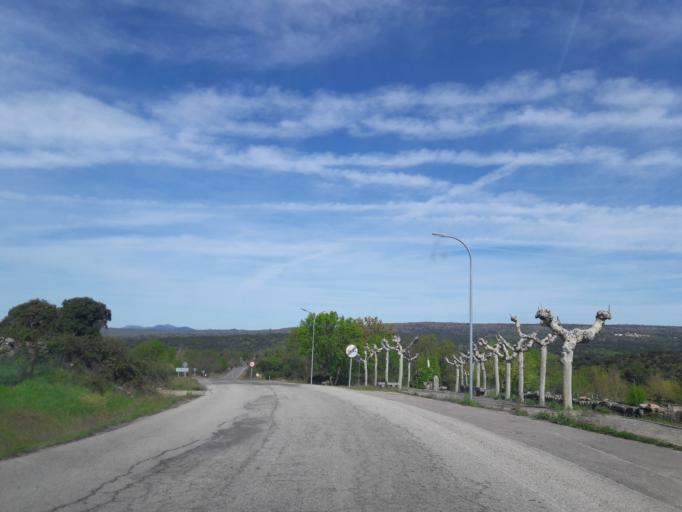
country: ES
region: Castille and Leon
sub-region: Provincia de Salamanca
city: Ledrada
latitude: 40.4715
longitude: -5.7216
